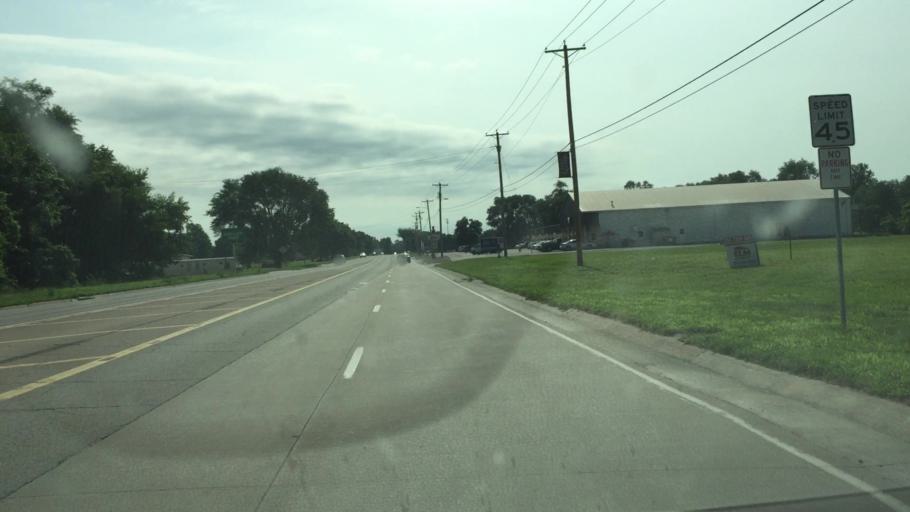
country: US
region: Iowa
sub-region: Lee County
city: Fort Madison
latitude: 40.6238
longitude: -91.3720
